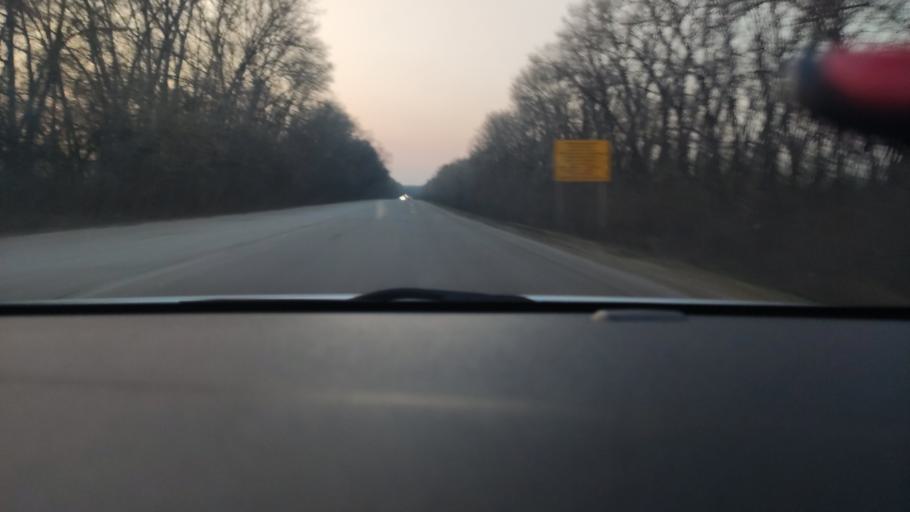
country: RU
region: Voronezj
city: Uryv-Pokrovka
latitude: 51.2182
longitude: 39.0674
